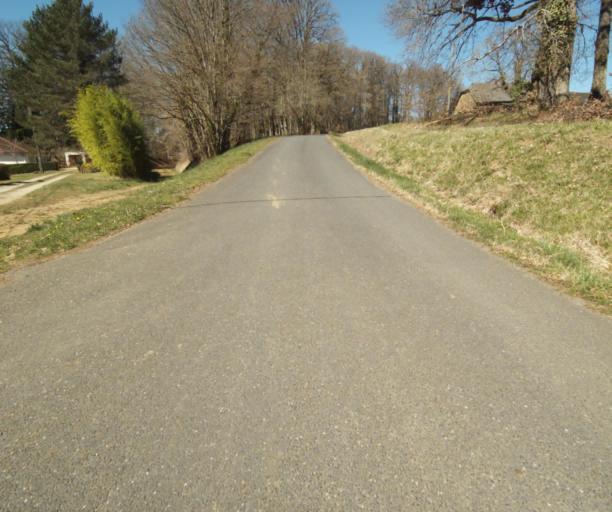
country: FR
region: Limousin
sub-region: Departement de la Correze
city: Seilhac
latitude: 45.3754
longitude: 1.6934
